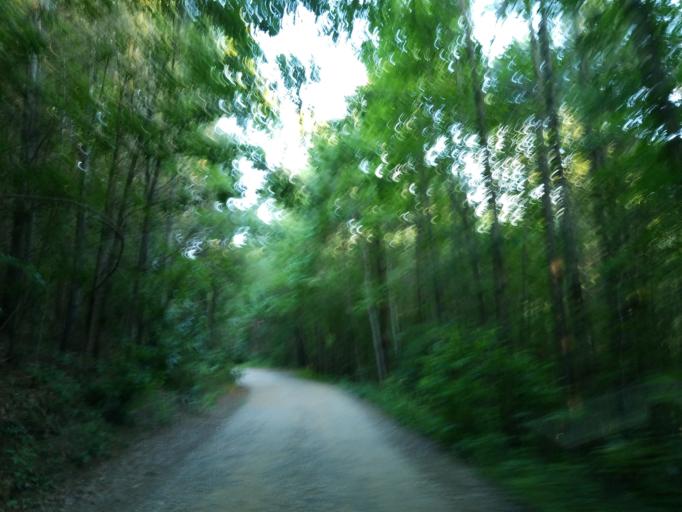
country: US
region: Georgia
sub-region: Fannin County
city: Blue Ridge
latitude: 34.7499
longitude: -84.1790
